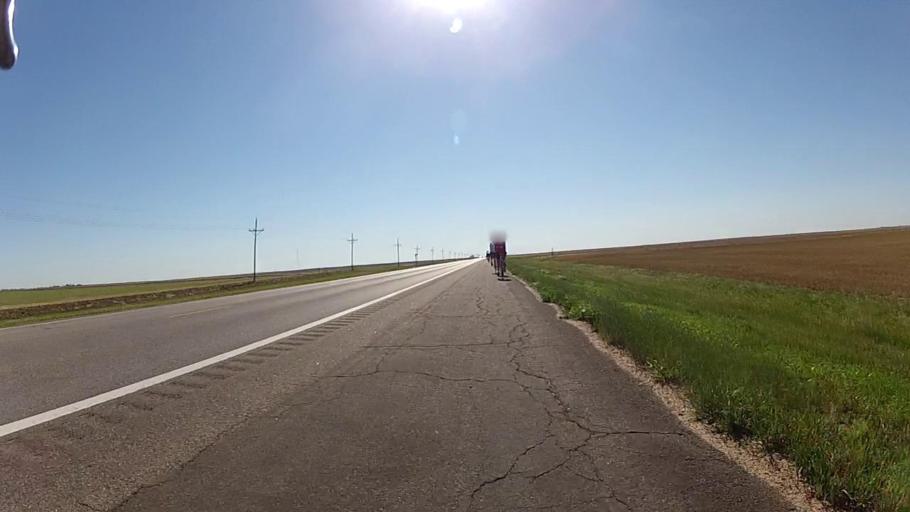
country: US
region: Kansas
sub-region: Kiowa County
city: Greensburg
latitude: 37.5862
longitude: -99.6320
